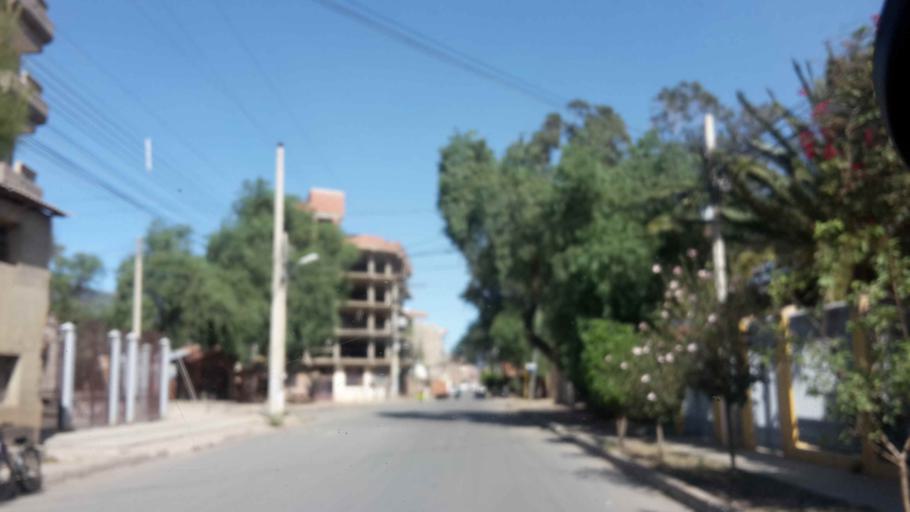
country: BO
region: Cochabamba
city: Cochabamba
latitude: -17.3376
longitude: -66.2243
